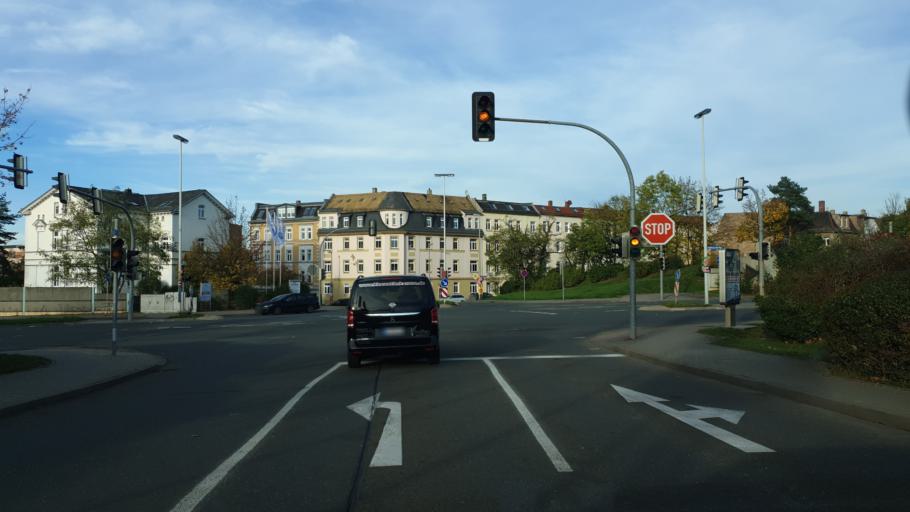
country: DE
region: Thuringia
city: Gera
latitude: 50.8617
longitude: 12.0867
